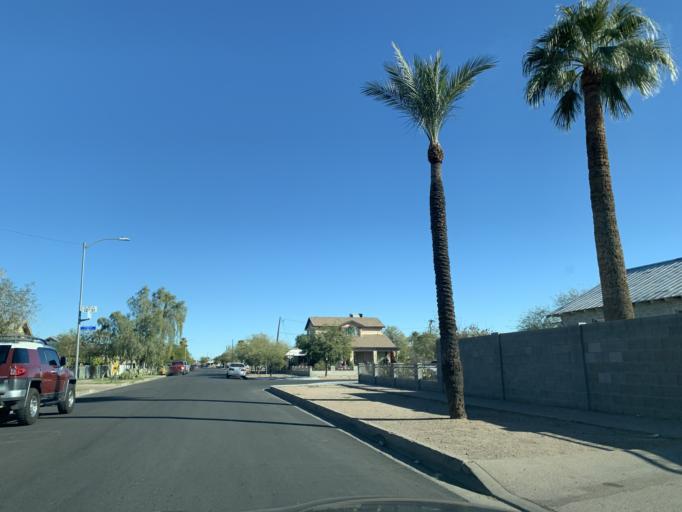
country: US
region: Arizona
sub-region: Maricopa County
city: Phoenix
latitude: 33.4539
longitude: -112.0564
